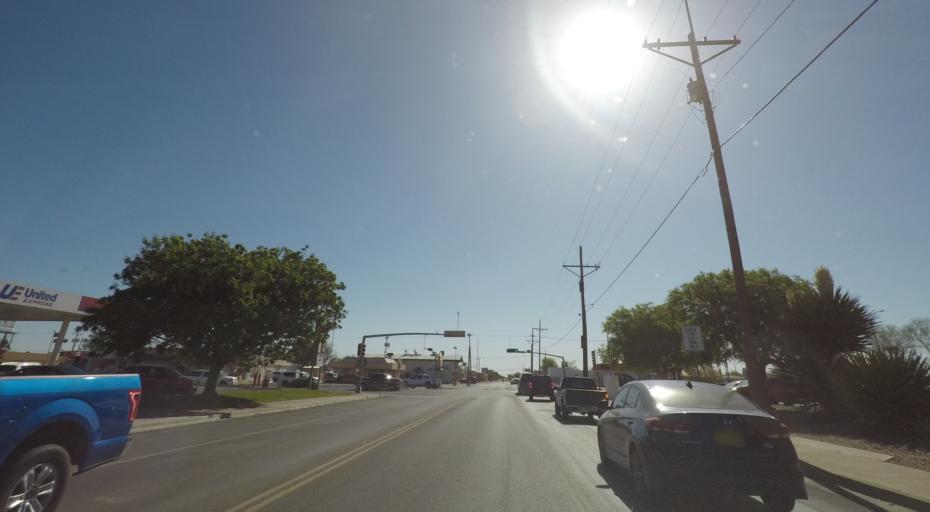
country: US
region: New Mexico
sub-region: Chaves County
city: Roswell
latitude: 33.3798
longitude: -104.5235
